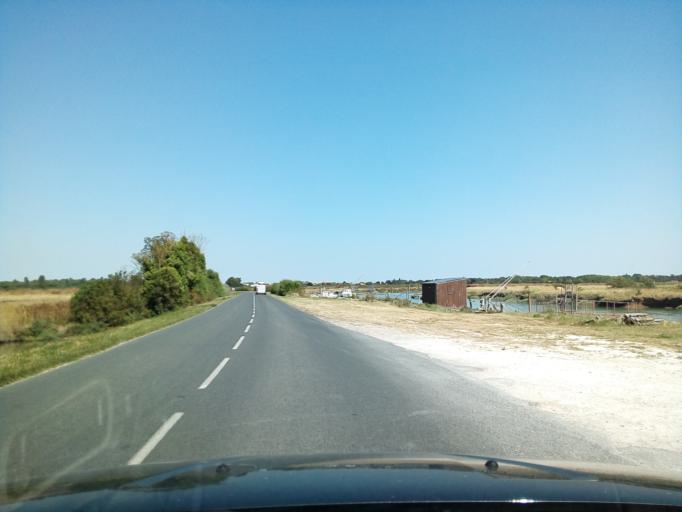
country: FR
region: Poitou-Charentes
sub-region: Departement de la Charente-Maritime
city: Boyard-Ville
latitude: 45.9660
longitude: -1.2588
